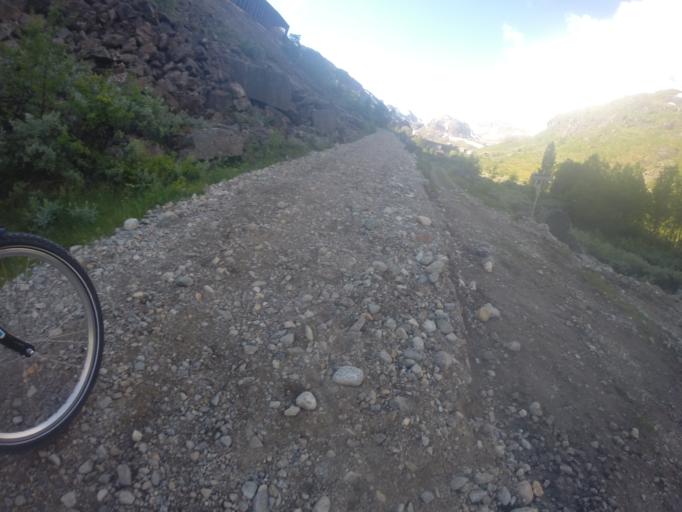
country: NO
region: Sogn og Fjordane
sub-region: Aurland
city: Aurlandsvangen
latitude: 60.7380
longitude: 7.1211
